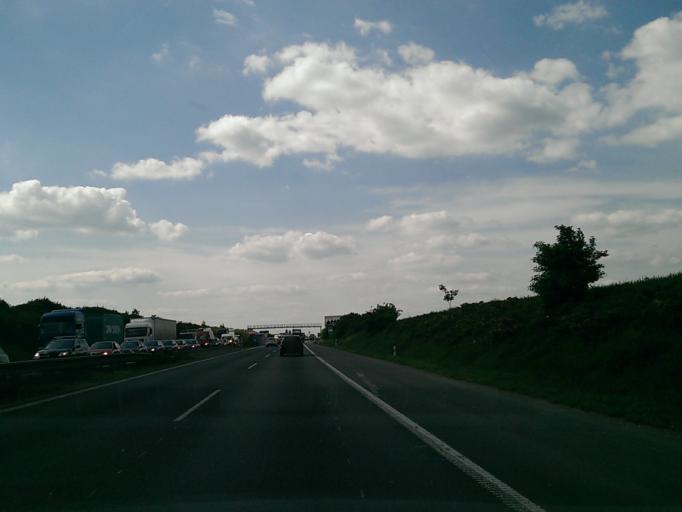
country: CZ
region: Central Bohemia
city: Zdiby
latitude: 50.1656
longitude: 14.4686
